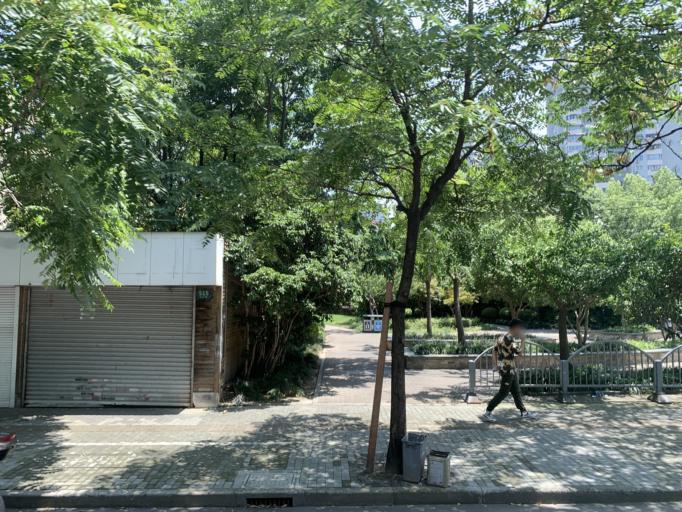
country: CN
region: Shanghai Shi
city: Huamu
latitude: 31.2470
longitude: 121.5772
